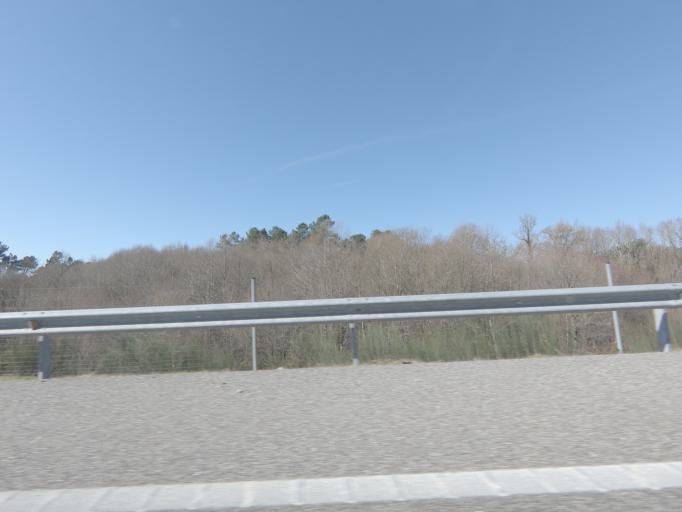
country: ES
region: Galicia
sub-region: Provincia de Ourense
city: Cea
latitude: 42.4688
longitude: -8.0278
